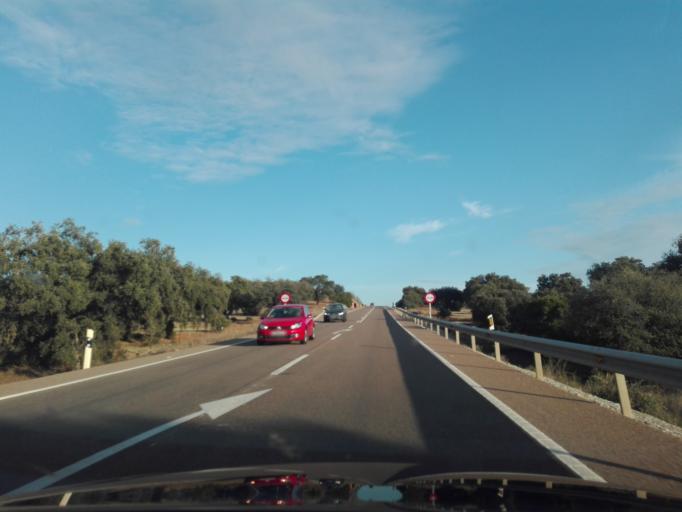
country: ES
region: Extremadura
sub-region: Provincia de Badajoz
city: Usagre
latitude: 38.3666
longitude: -6.2362
